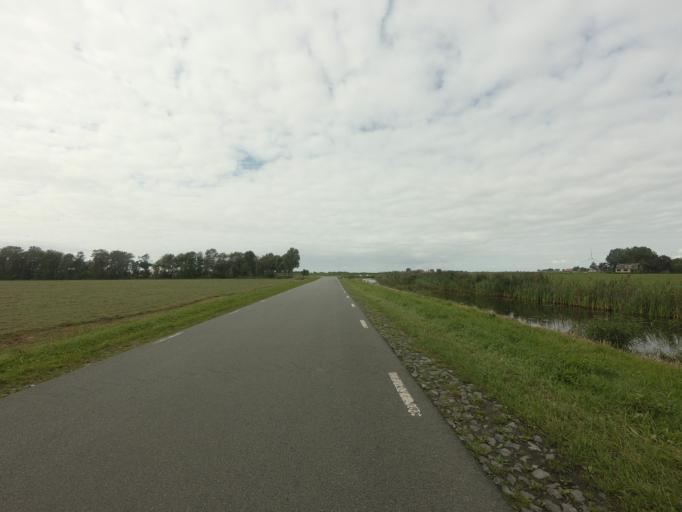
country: NL
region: Friesland
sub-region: Sudwest Fryslan
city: Workum
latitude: 52.9665
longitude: 5.4823
